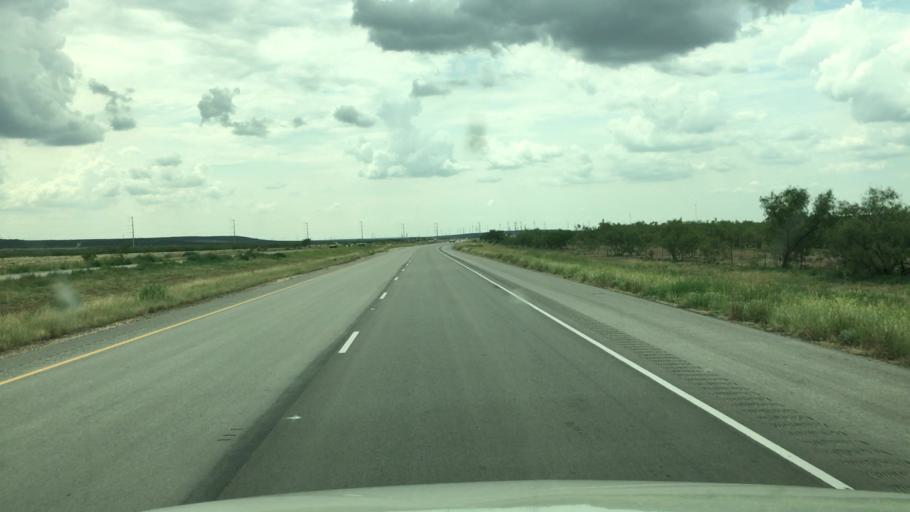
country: US
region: Texas
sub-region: Sterling County
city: Sterling City
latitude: 31.9628
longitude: -101.2196
